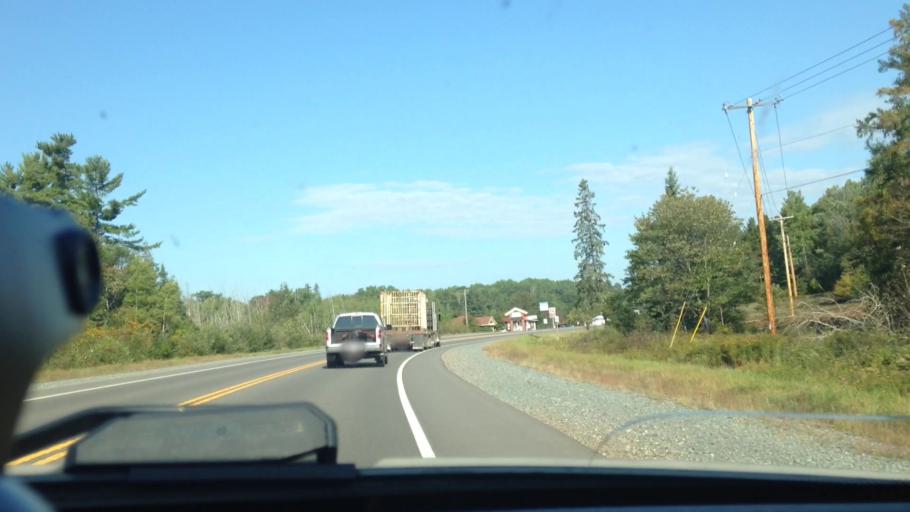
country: US
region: Michigan
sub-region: Dickinson County
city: Iron Mountain
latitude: 45.8671
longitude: -88.0801
